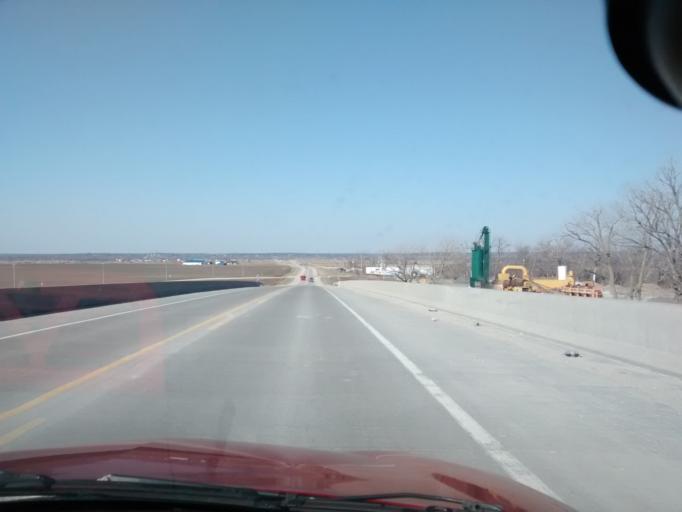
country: US
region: Iowa
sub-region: Pottawattamie County
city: Carter Lake
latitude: 41.3600
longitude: -95.8801
